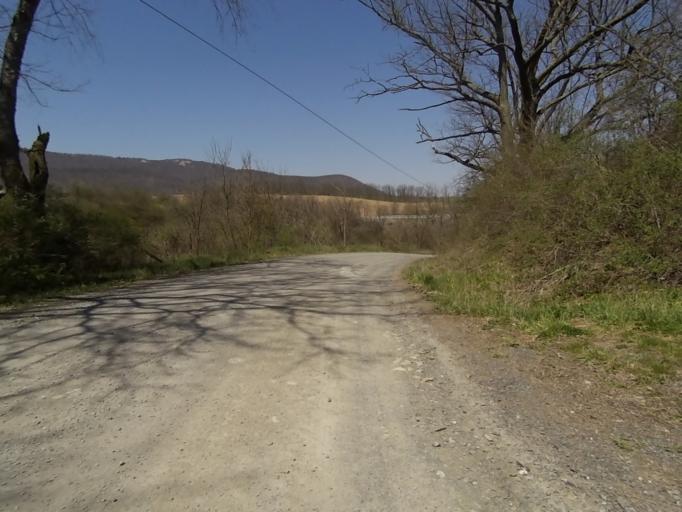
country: US
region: Pennsylvania
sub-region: Blair County
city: Williamsburg
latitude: 40.5584
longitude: -78.1553
